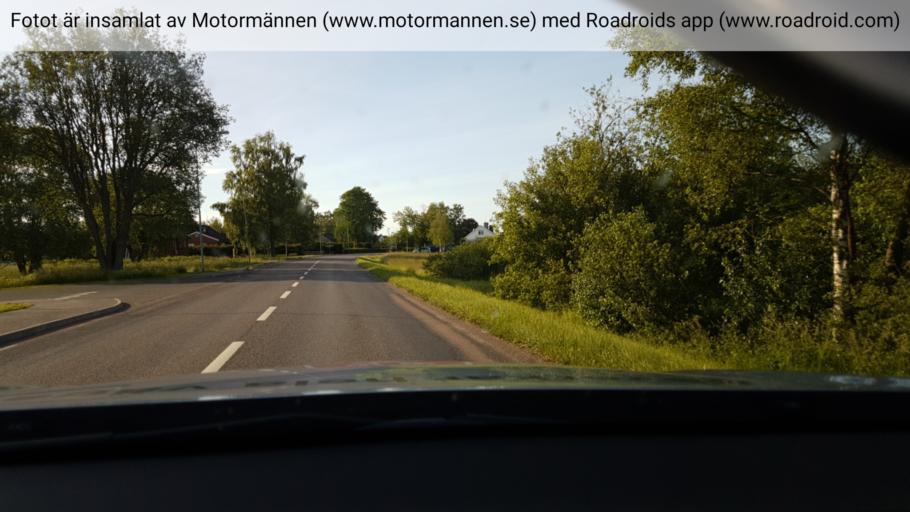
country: SE
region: Vaestra Goetaland
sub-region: Falkopings Kommun
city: Falkoeping
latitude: 58.0801
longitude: 13.5167
